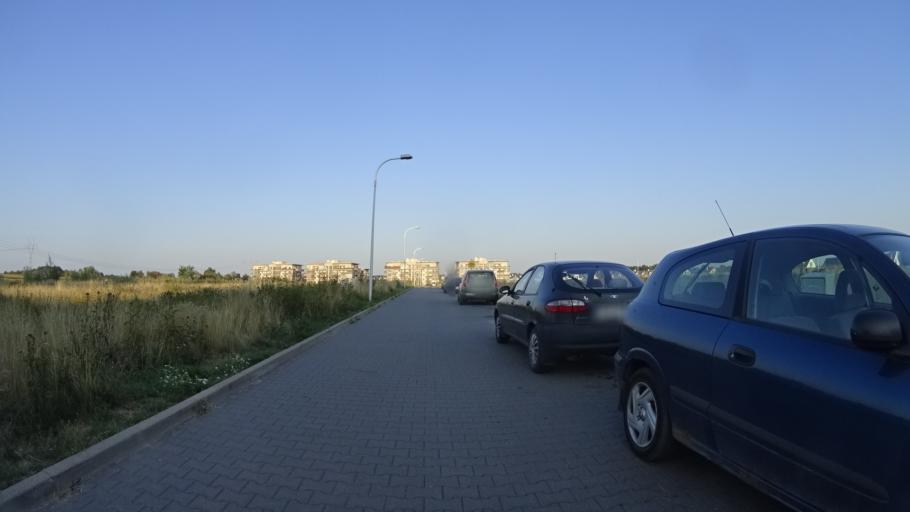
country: PL
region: Masovian Voivodeship
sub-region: Powiat warszawski zachodni
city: Ozarow Mazowiecki
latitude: 52.2360
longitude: 20.7739
